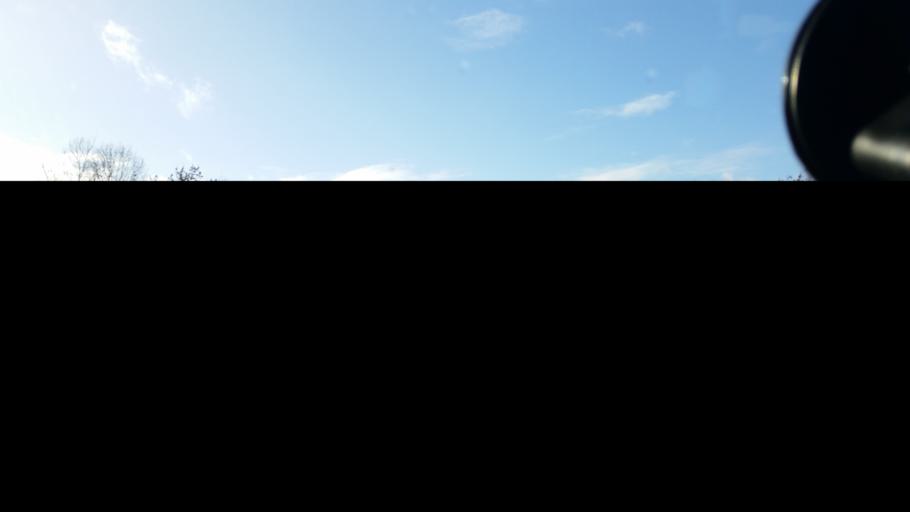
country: IE
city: Kentstown
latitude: 53.6004
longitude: -6.4702
